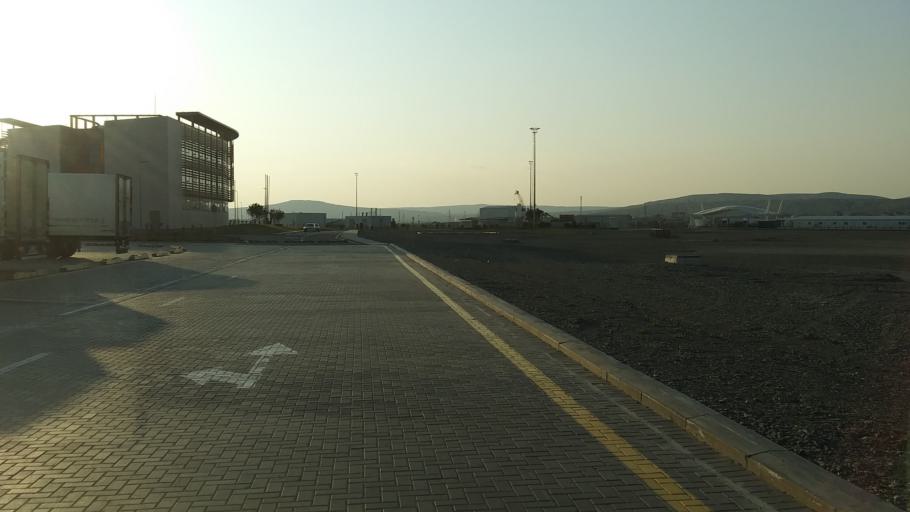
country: AZ
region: Baki
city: Qobustan
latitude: 39.9784
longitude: 49.4454
